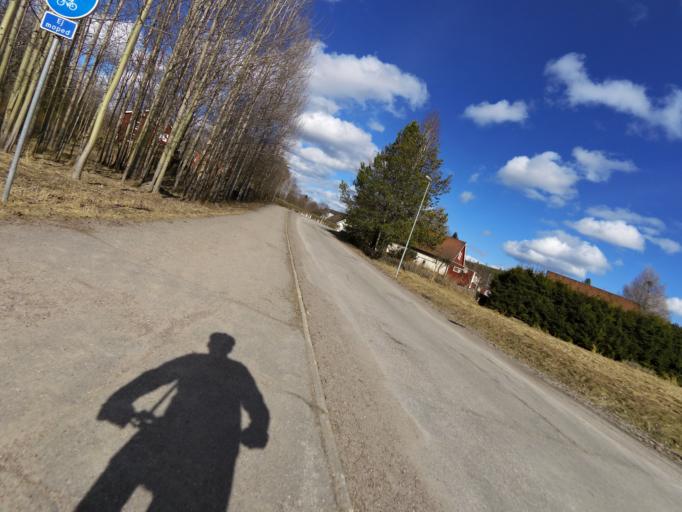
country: SE
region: Gaevleborg
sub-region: Hofors Kommun
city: Hofors
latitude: 60.5376
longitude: 16.3076
